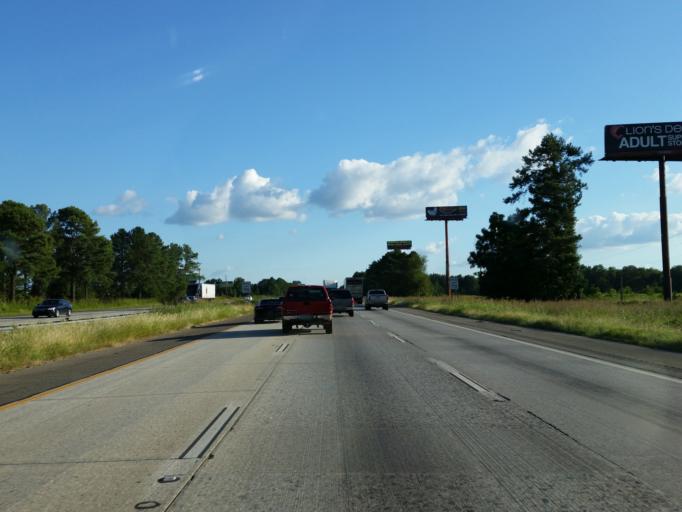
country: US
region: Georgia
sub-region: Peach County
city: Byron
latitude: 32.6500
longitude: -83.7441
